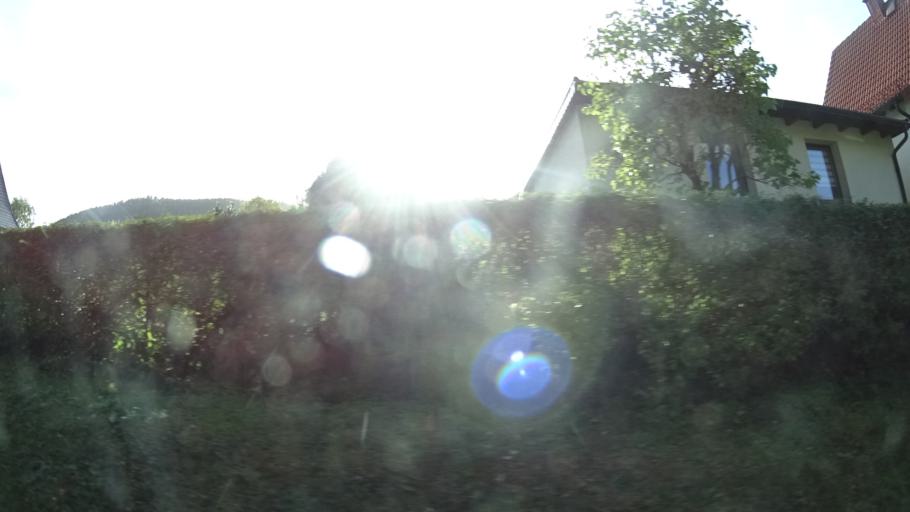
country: DE
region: Thuringia
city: Bermbach
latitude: 50.7114
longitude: 10.6175
